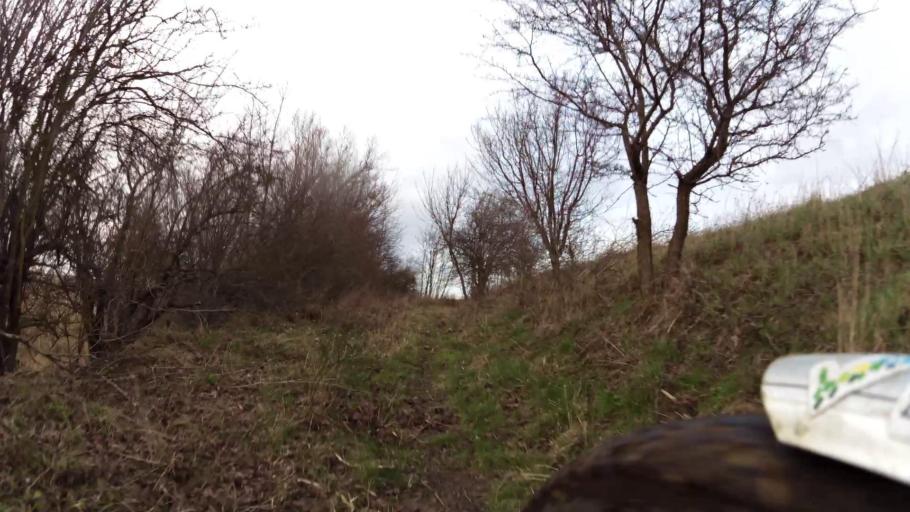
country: PL
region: West Pomeranian Voivodeship
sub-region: Powiat kamienski
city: Kamien Pomorski
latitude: 53.9358
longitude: 14.7621
